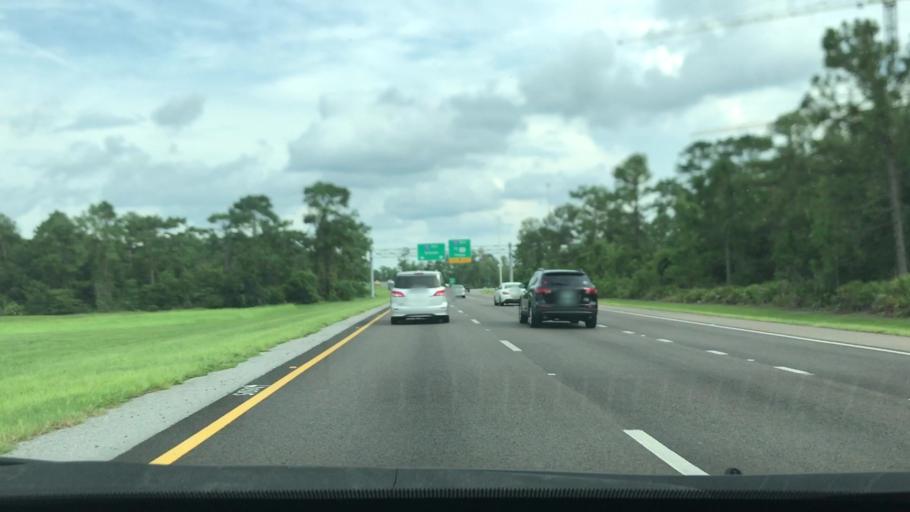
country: US
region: Florida
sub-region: Osceola County
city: Celebration
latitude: 28.3609
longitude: -81.5264
